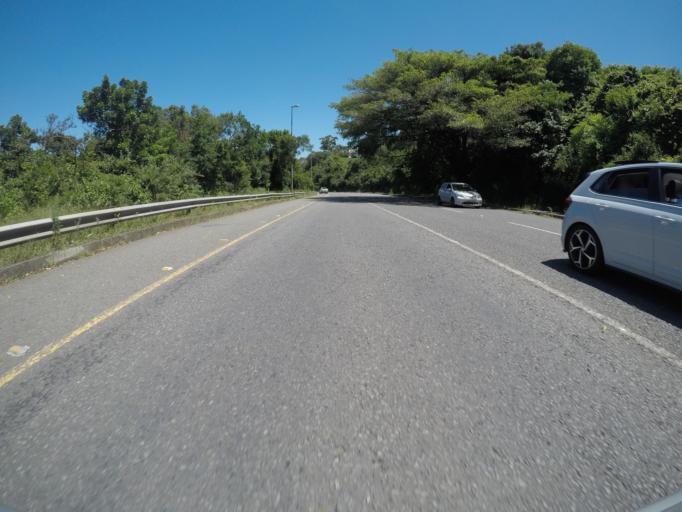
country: ZA
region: Eastern Cape
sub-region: Buffalo City Metropolitan Municipality
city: East London
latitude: -32.9675
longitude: 27.9309
